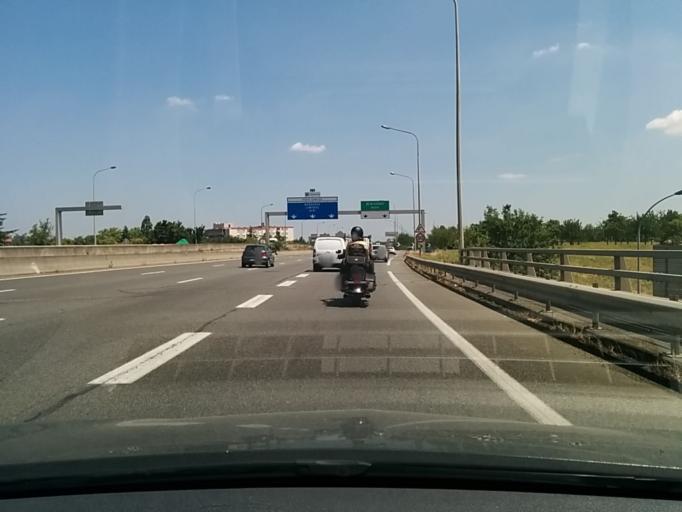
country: FR
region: Midi-Pyrenees
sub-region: Departement de la Haute-Garonne
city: Blagnac
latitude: 43.6039
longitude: 1.4016
